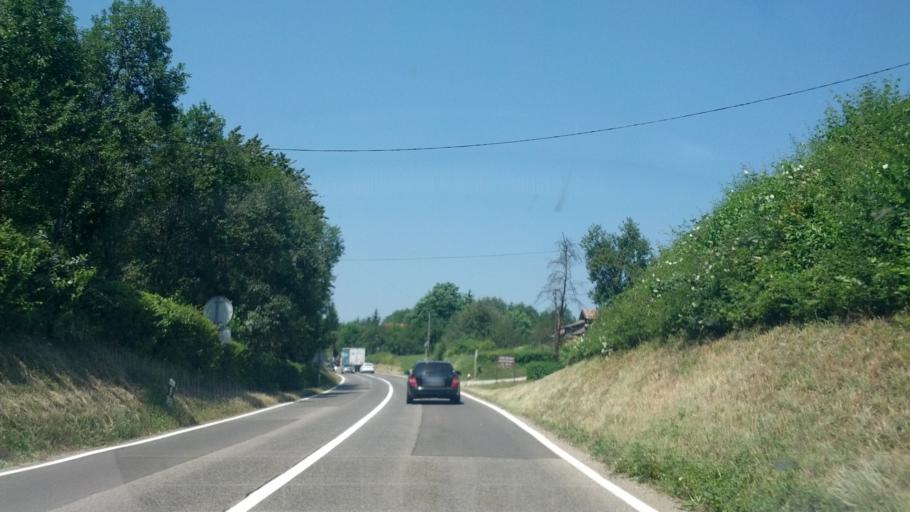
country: HR
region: Karlovacka
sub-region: Grad Karlovac
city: Slunj
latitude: 45.1251
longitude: 15.5754
